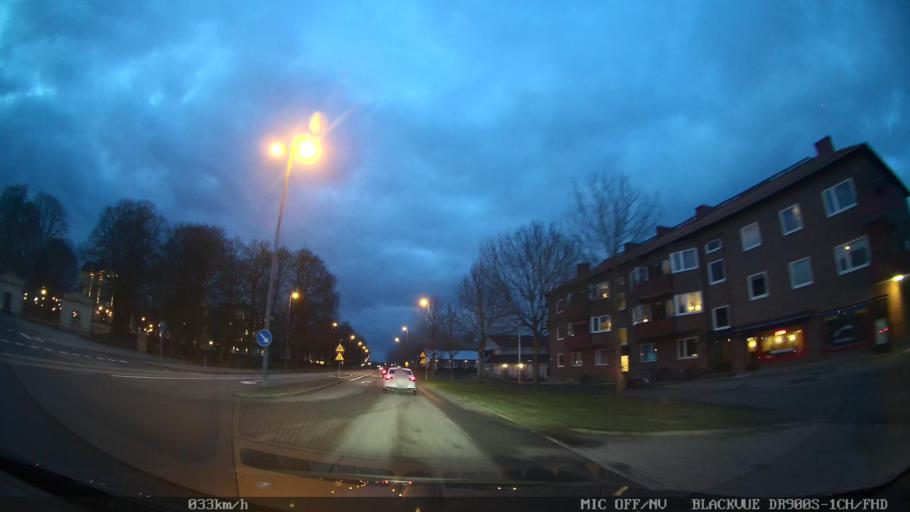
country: SE
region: Skane
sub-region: Hassleholms Kommun
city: Hassleholm
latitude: 56.1645
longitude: 13.7584
